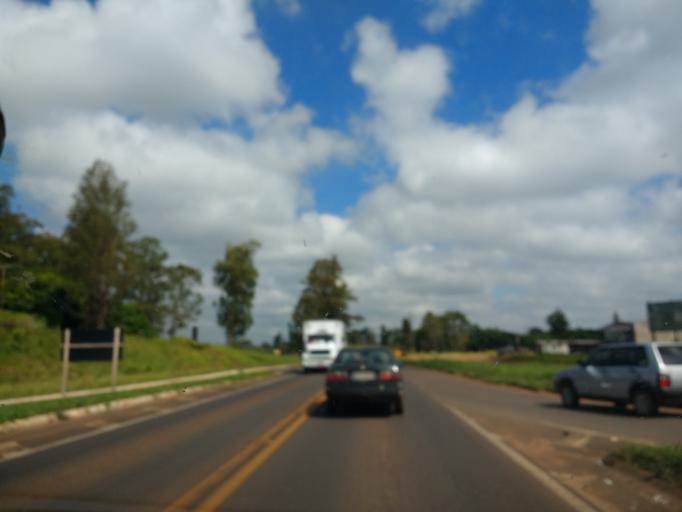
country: BR
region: Parana
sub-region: Cruzeiro Do Oeste
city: Cruzeiro do Oeste
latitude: -23.7953
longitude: -53.0477
